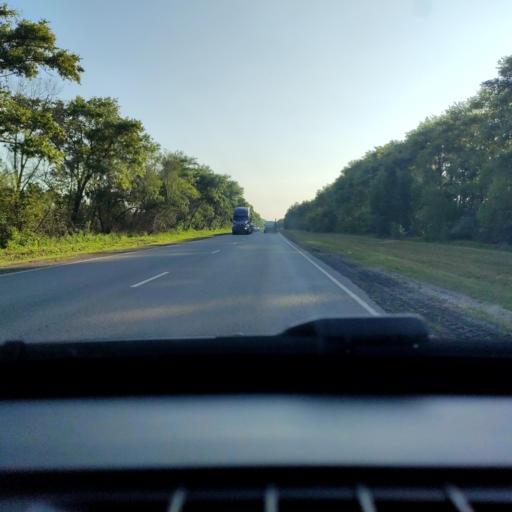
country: RU
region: Voronezj
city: Kashirskoye
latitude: 51.4643
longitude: 39.8509
